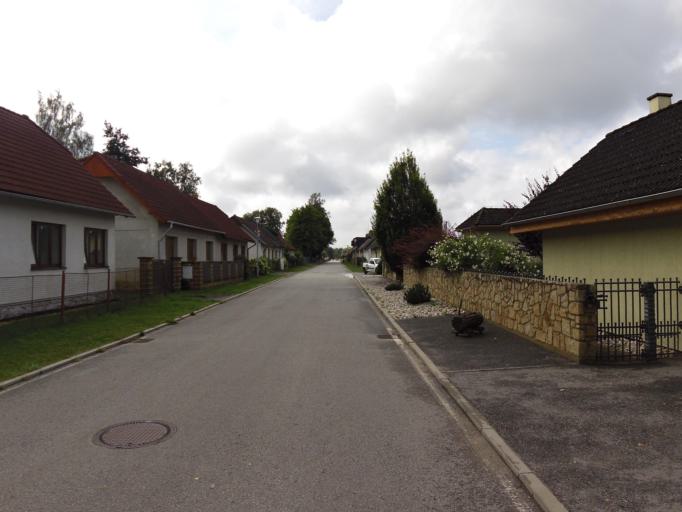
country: CZ
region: Jihocesky
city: Suchdol nad Luznici
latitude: 48.9112
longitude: 14.9162
